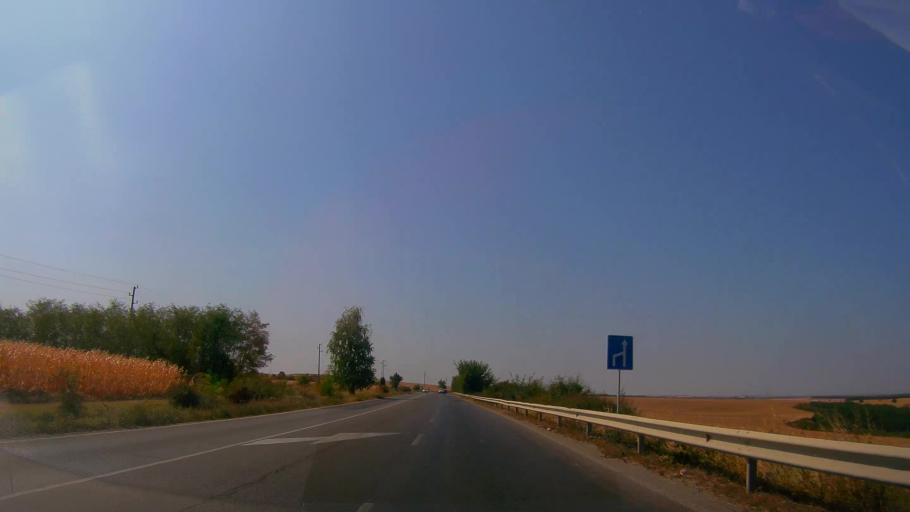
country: BG
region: Ruse
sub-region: Obshtina Vetovo
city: Senovo
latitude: 43.5621
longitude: 26.3583
